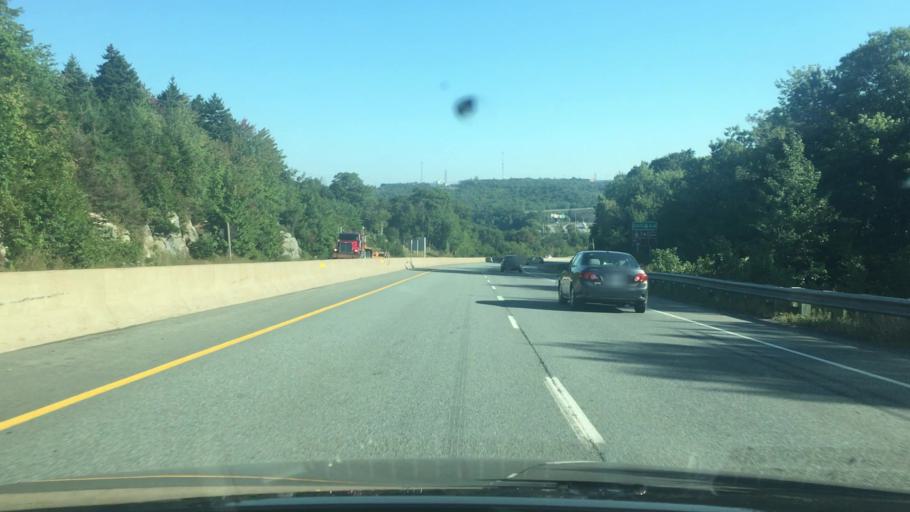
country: CA
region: Nova Scotia
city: Dartmouth
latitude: 44.7383
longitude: -63.6613
